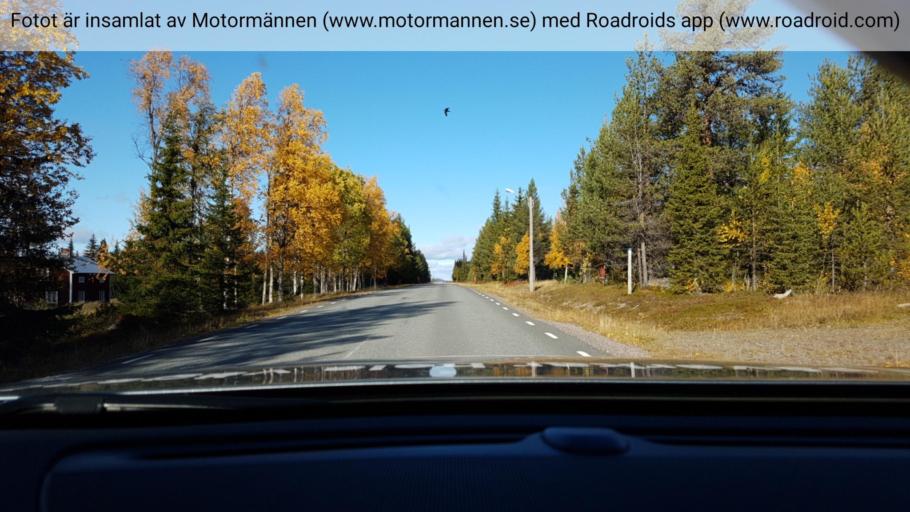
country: SE
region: Vaesterbotten
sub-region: Mala Kommun
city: Mala
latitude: 65.7869
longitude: 18.4923
